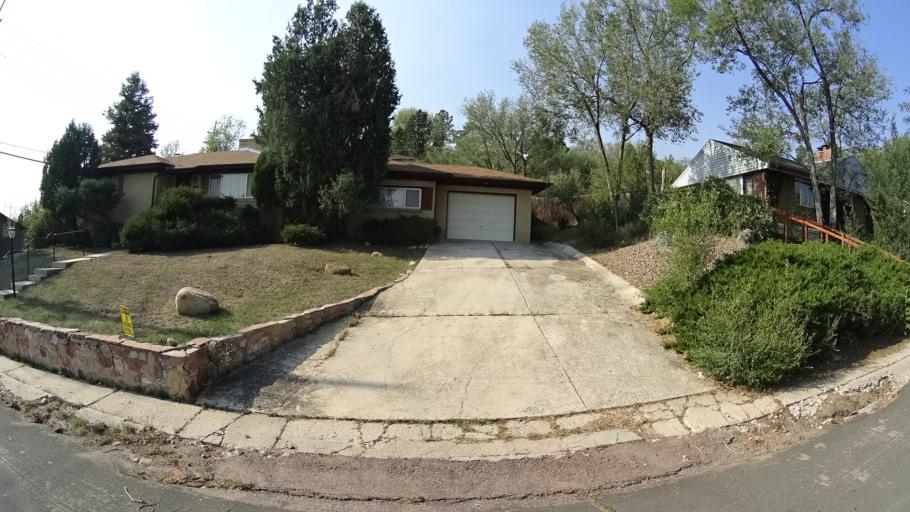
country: US
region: Colorado
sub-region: El Paso County
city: Colorado Springs
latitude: 38.8117
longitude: -104.8504
